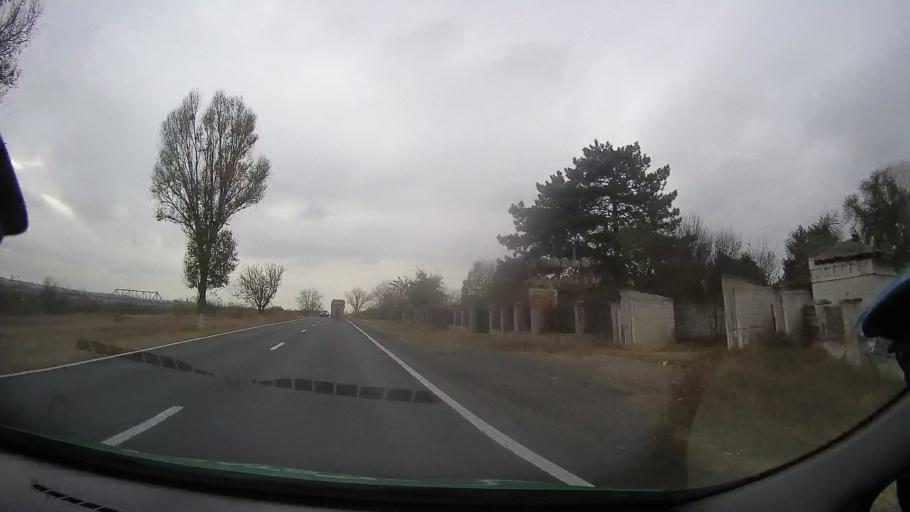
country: RO
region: Constanta
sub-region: Comuna Castelu
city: Castelu
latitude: 44.2530
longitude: 28.3256
